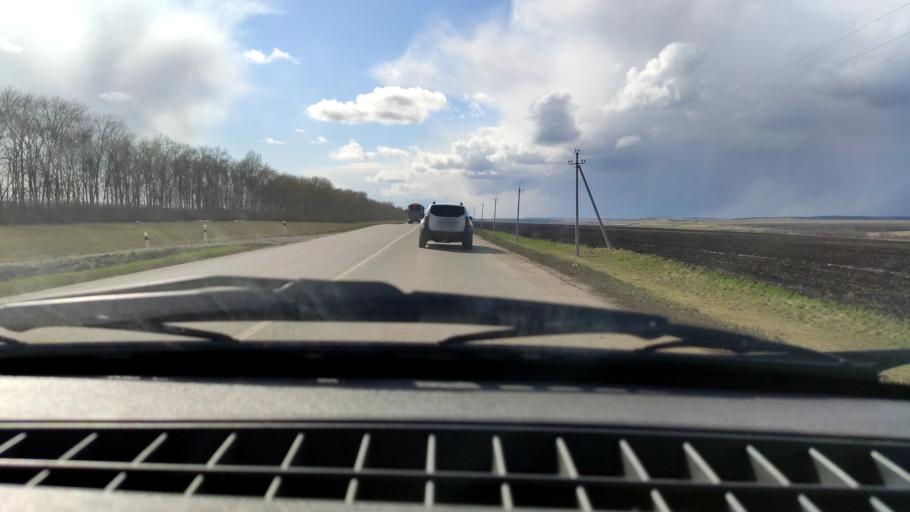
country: RU
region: Bashkortostan
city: Chekmagush
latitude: 55.1126
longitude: 54.8955
